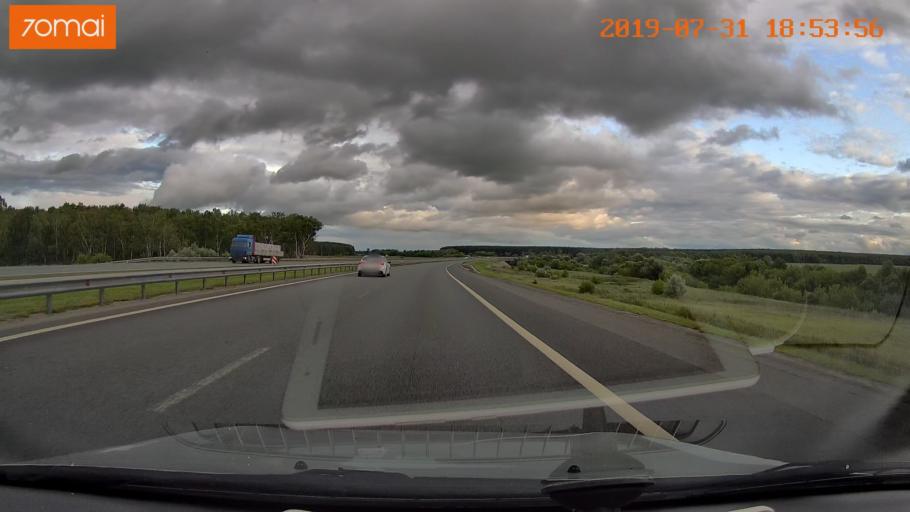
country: RU
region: Moskovskaya
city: Raduzhnyy
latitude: 55.1965
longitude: 38.6637
